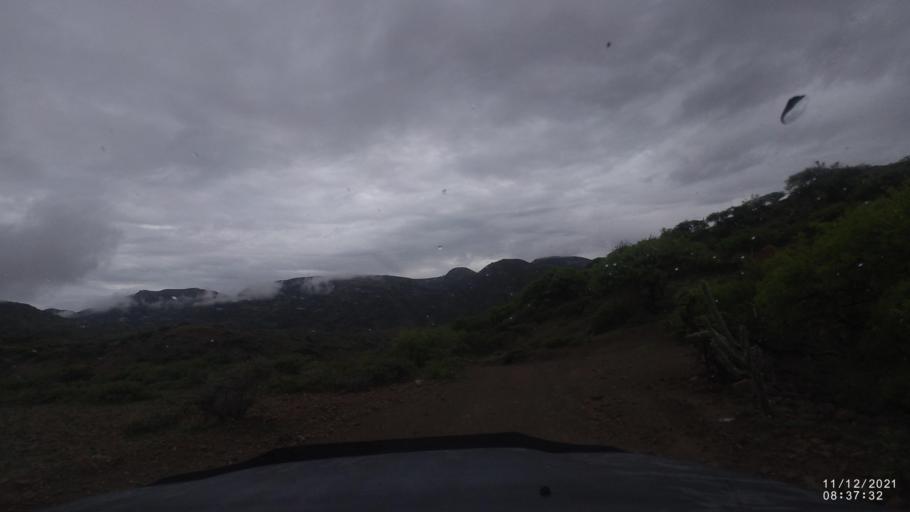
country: BO
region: Cochabamba
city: Tarata
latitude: -17.9260
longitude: -65.9372
